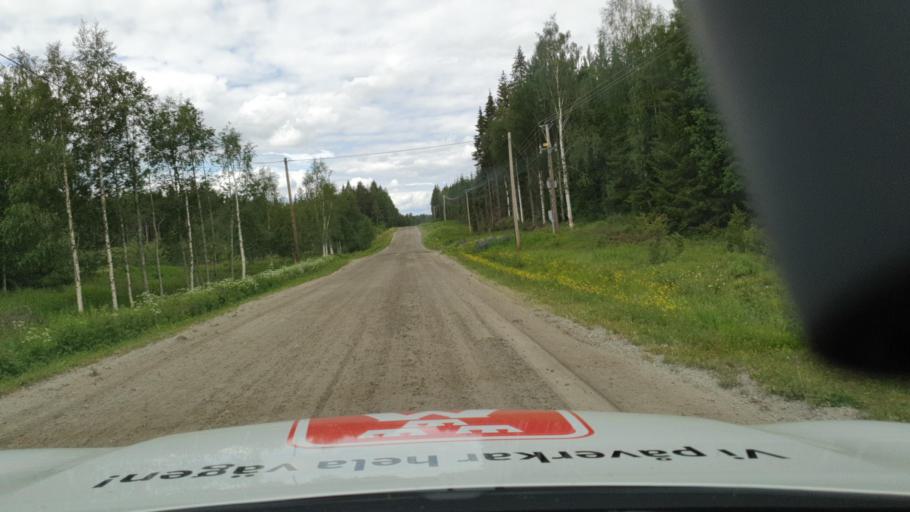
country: SE
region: Vaesterbotten
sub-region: Bjurholms Kommun
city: Bjurholm
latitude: 63.8472
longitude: 18.9870
